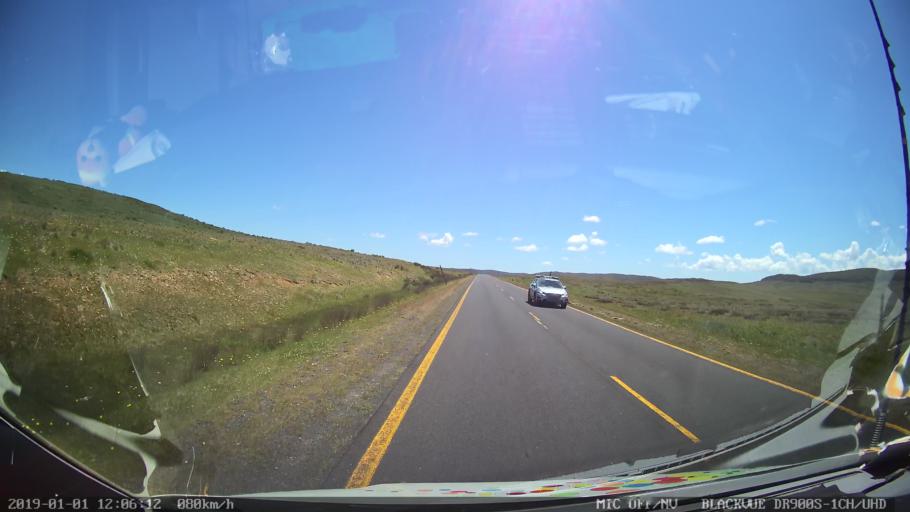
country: AU
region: New South Wales
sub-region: Snowy River
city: Jindabyne
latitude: -35.8478
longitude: 148.4912
